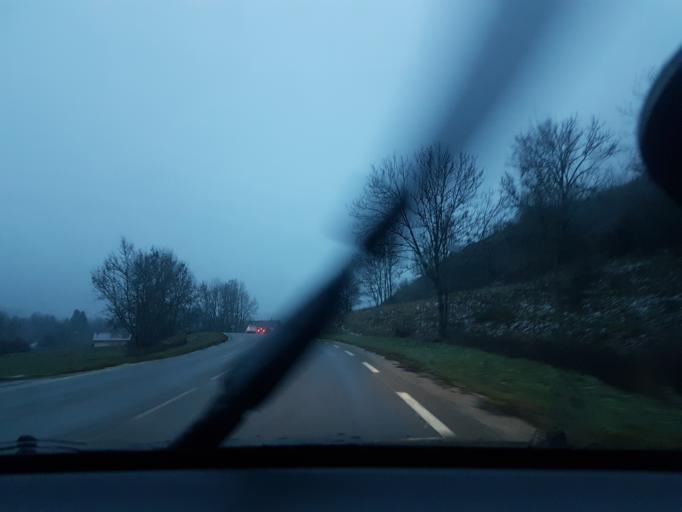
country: FR
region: Franche-Comte
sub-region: Departement du Doubs
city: La Cluse-et-Mijoux
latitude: 46.8729
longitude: 6.3930
